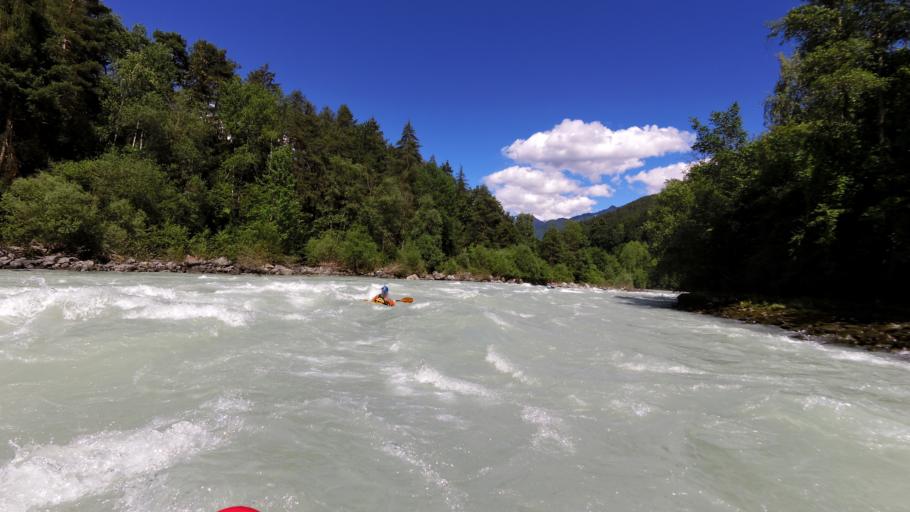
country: AT
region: Tyrol
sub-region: Politischer Bezirk Imst
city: Roppen
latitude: 47.2122
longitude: 10.8035
